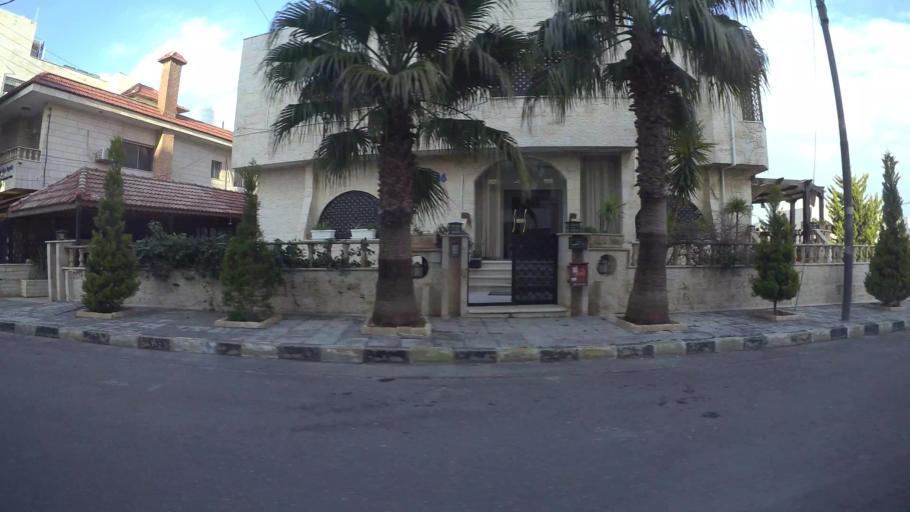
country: JO
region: Amman
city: Al Jubayhah
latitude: 32.0050
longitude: 35.8680
